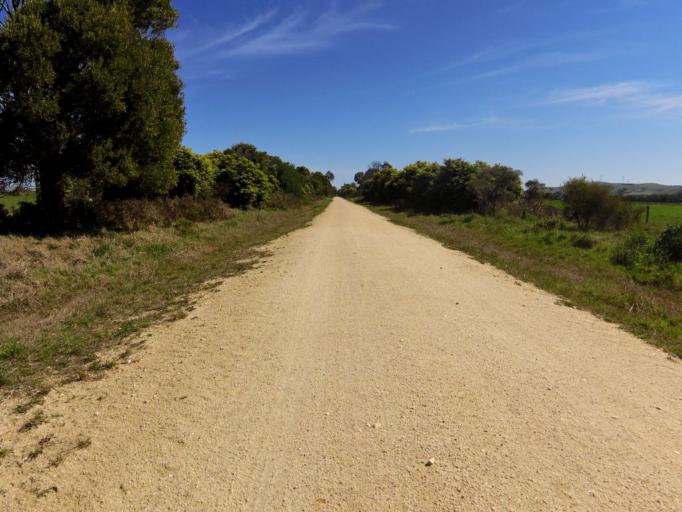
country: AU
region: Victoria
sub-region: Latrobe
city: Morwell
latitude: -38.6702
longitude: 146.4171
